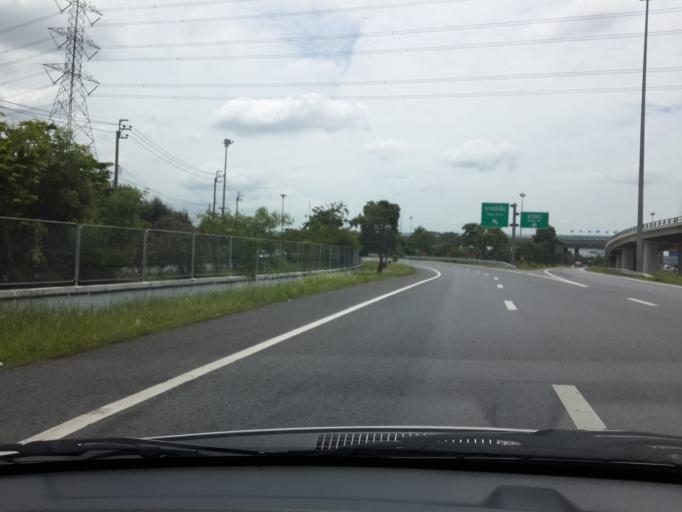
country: TH
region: Bangkok
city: Saphan Sung
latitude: 13.7332
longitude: 100.7002
